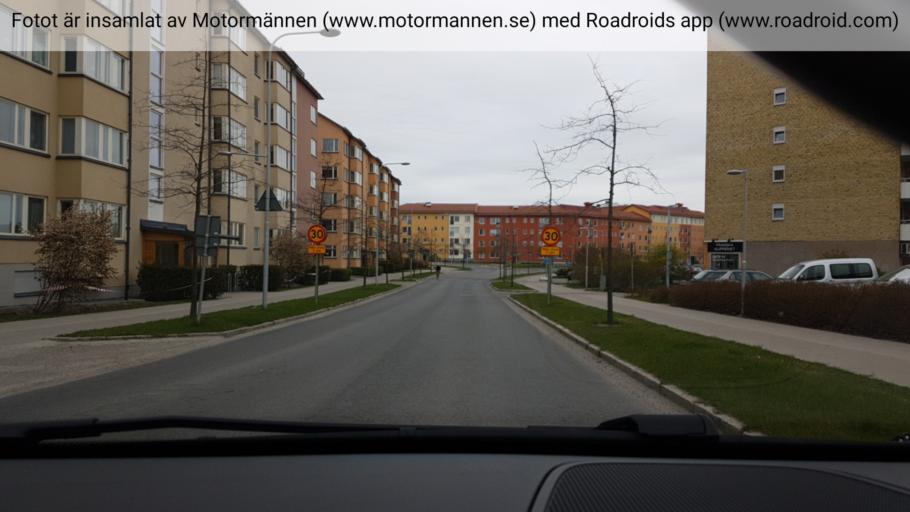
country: SE
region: Stockholm
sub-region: Huddinge Kommun
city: Huddinge
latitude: 59.2395
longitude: 17.9950
